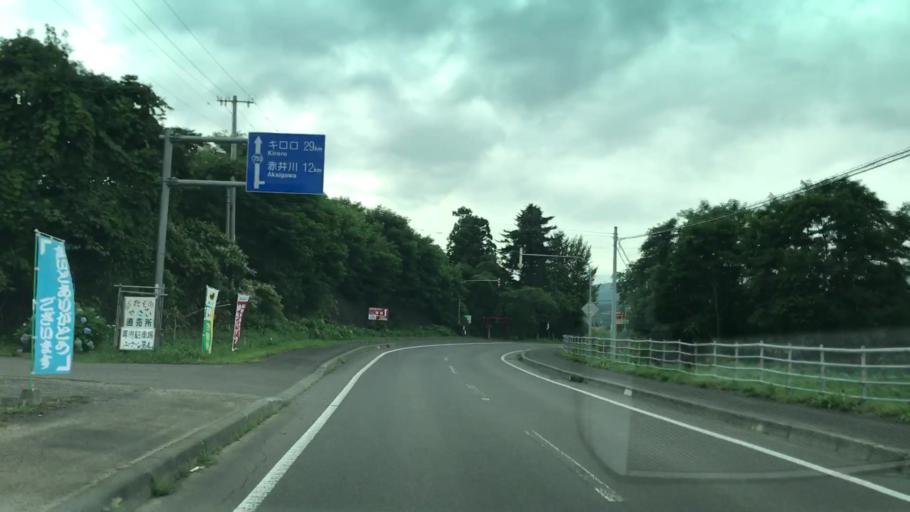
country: JP
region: Hokkaido
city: Yoichi
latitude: 43.1657
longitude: 140.8217
